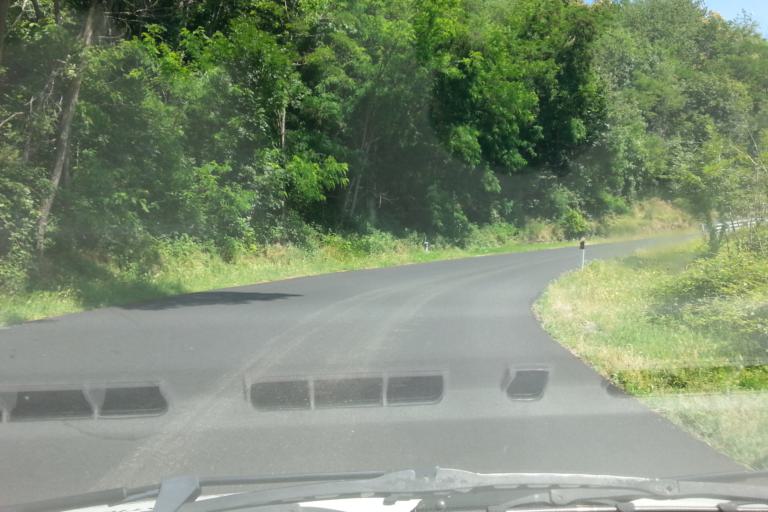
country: IT
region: Piedmont
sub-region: Provincia di Torino
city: Giaglione
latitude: 45.1416
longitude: 7.0053
